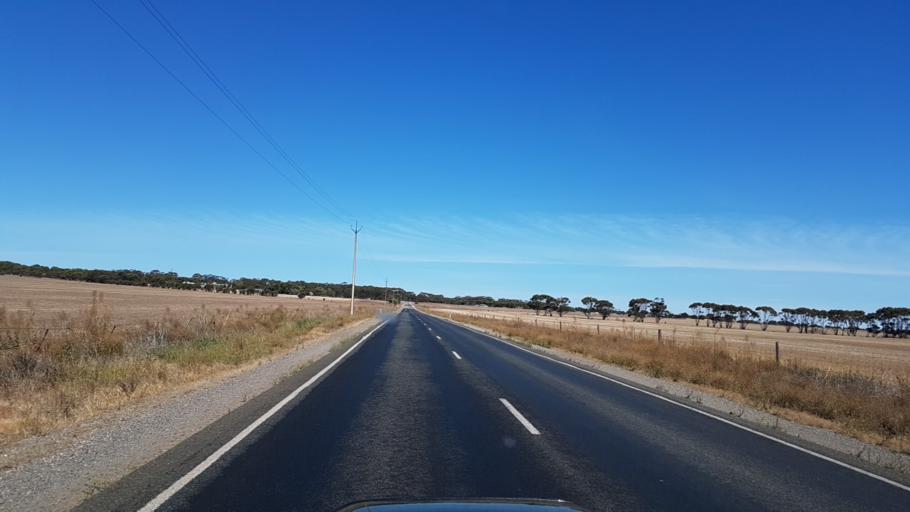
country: AU
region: South Australia
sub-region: Yorke Peninsula
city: Maitland
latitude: -34.3584
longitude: 137.6656
